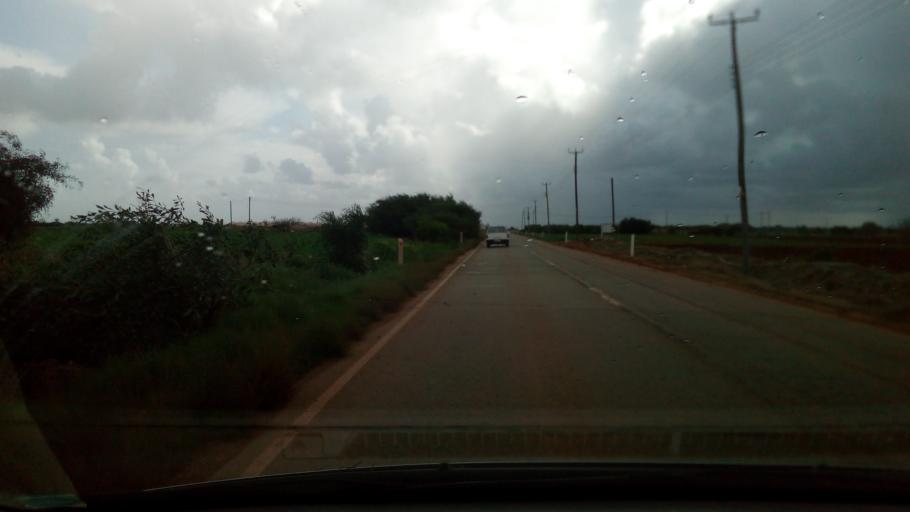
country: CY
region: Ammochostos
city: Liopetri
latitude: 34.9890
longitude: 33.8931
